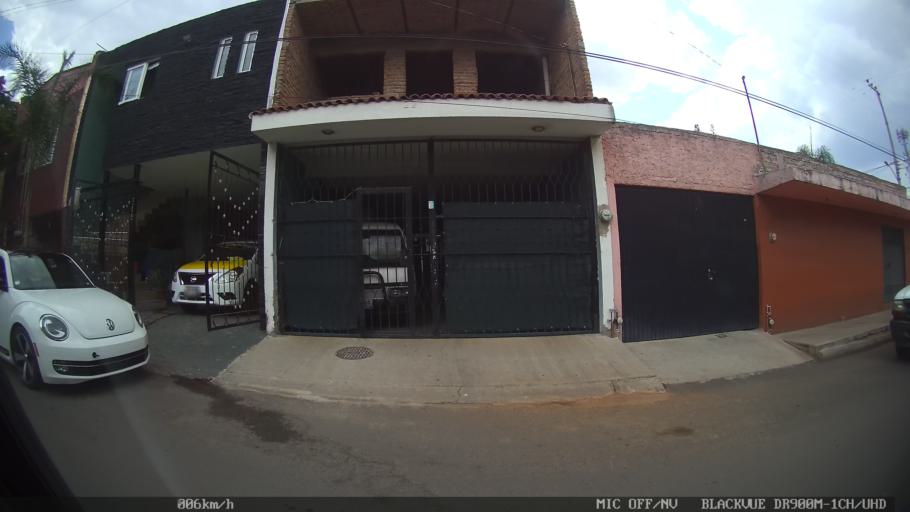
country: MX
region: Jalisco
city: Tlaquepaque
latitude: 20.6319
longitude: -103.2715
